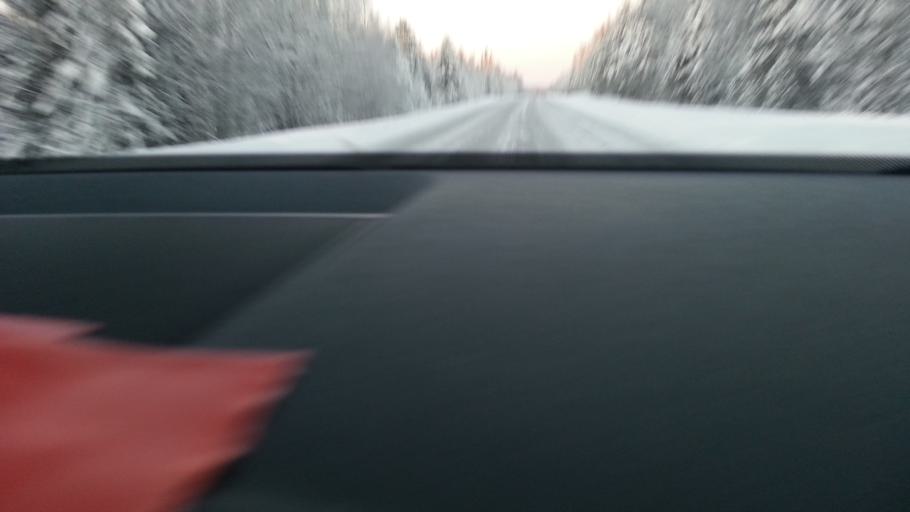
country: FI
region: Lapland
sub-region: Tunturi-Lappi
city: Kittilae
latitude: 67.2193
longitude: 24.9238
